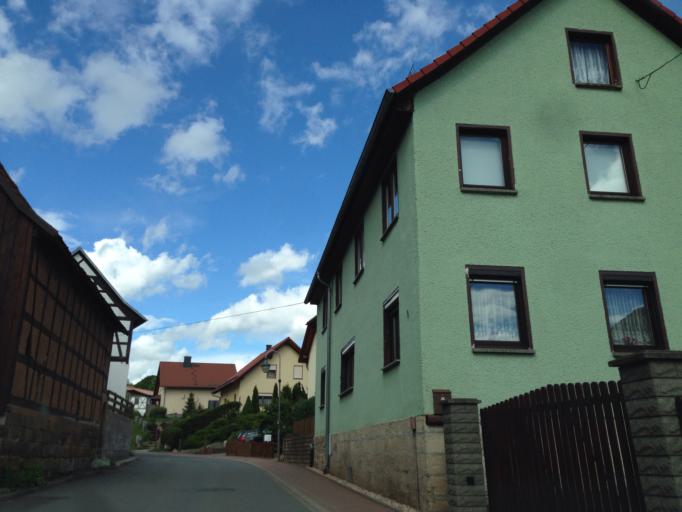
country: DE
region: Thuringia
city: Rudolstadt
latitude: 50.7746
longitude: 11.3572
